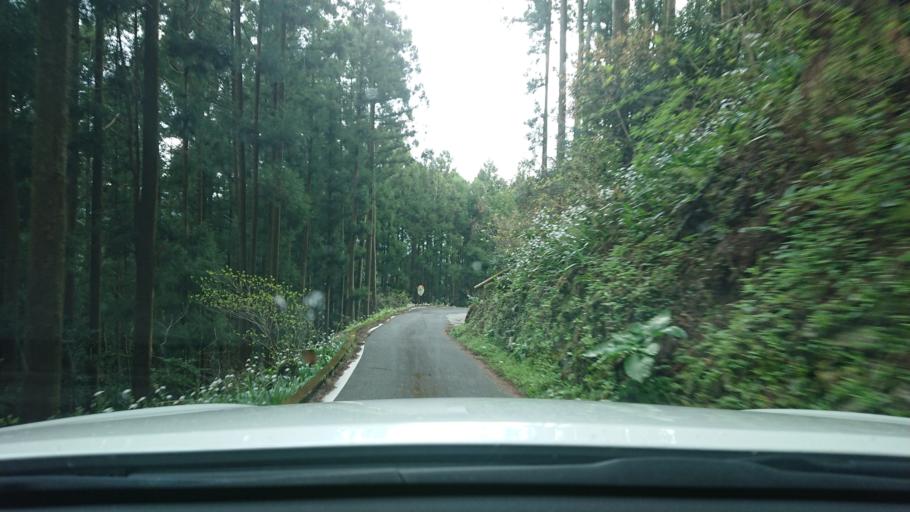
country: JP
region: Tokushima
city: Kamojimacho-jogejima
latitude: 33.8869
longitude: 134.3878
